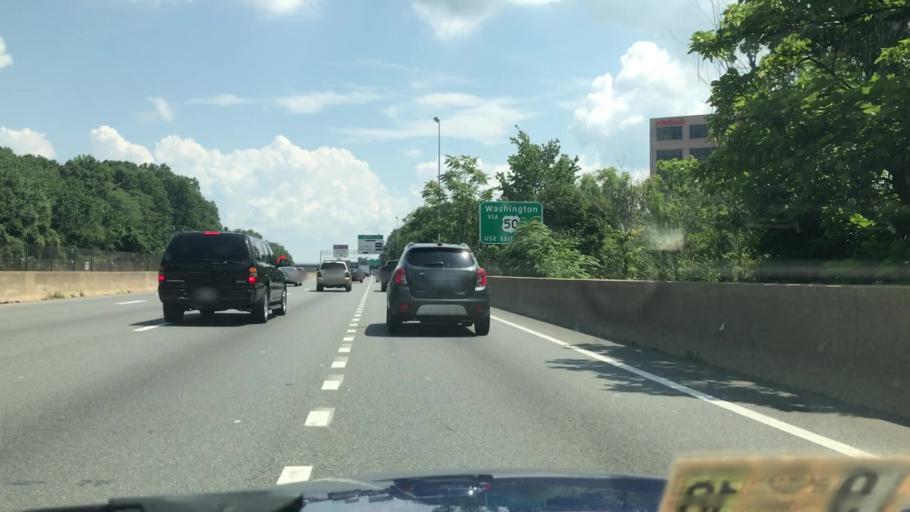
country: US
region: Virginia
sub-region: Fairfax County
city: Merrifield
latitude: 38.8809
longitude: -77.2353
